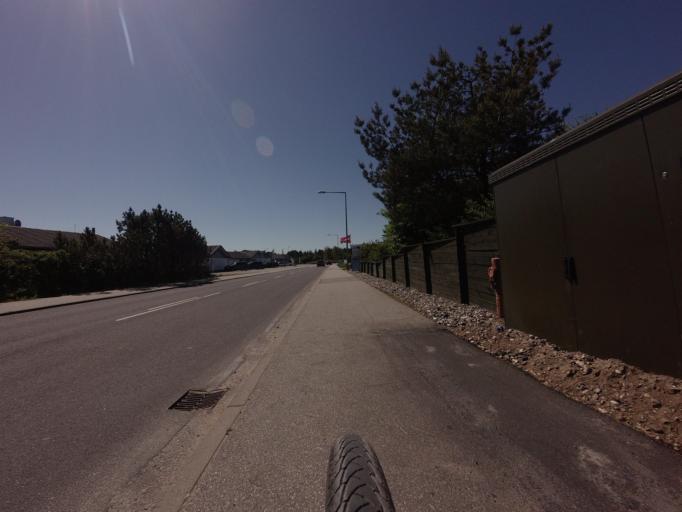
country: DK
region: North Denmark
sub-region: Jammerbugt Kommune
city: Pandrup
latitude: 57.2491
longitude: 9.6233
